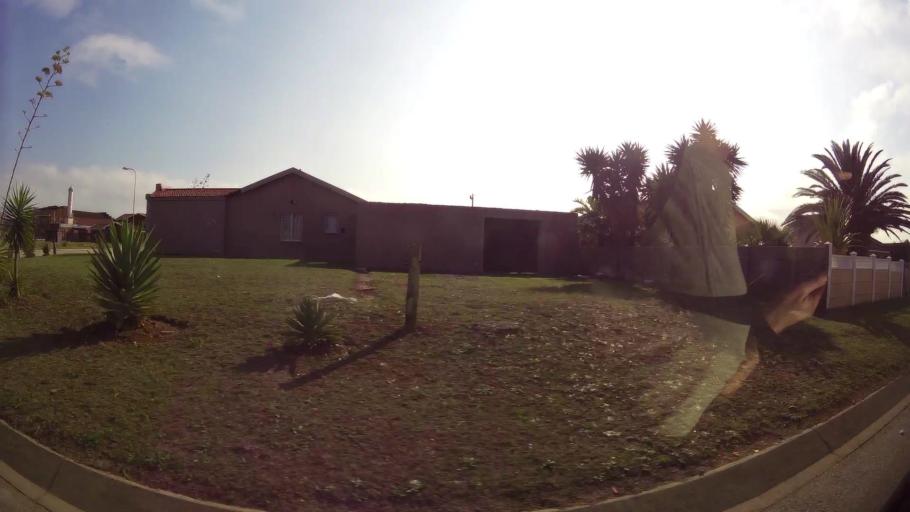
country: ZA
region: Eastern Cape
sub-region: Nelson Mandela Bay Metropolitan Municipality
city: Port Elizabeth
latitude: -33.9240
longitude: 25.5282
